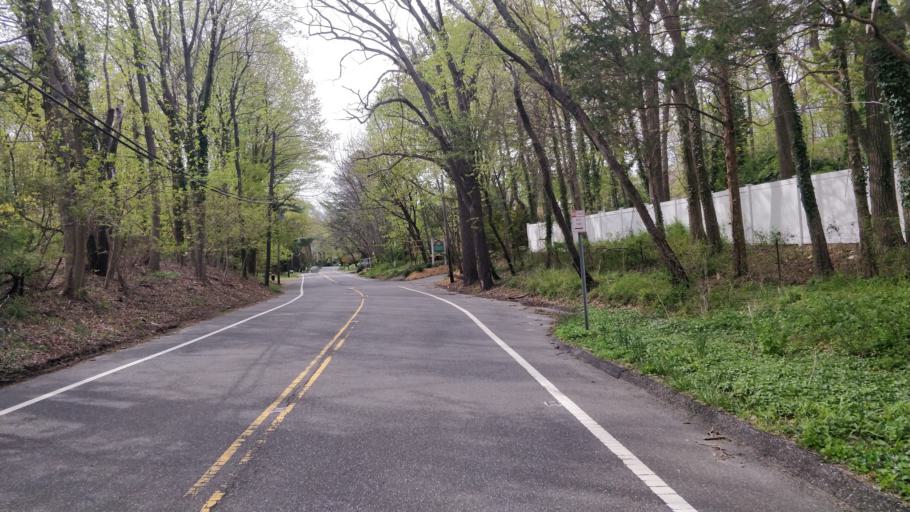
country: US
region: New York
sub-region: Suffolk County
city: Setauket-East Setauket
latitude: 40.9342
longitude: -73.0961
